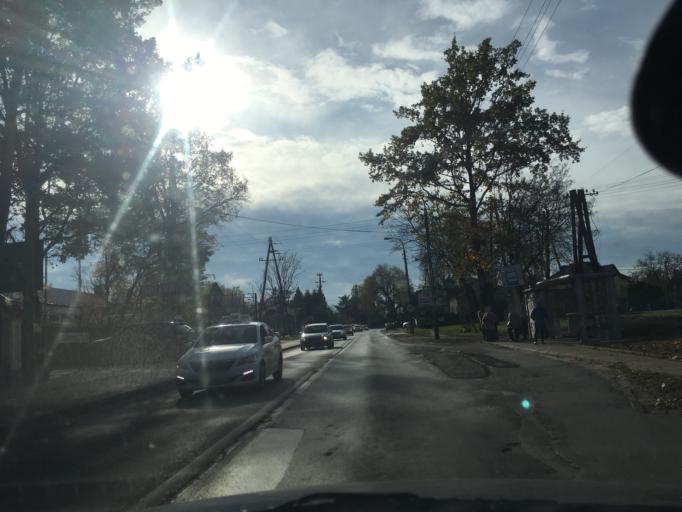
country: PL
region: Masovian Voivodeship
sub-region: Powiat piaseczynski
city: Piaseczno
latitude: 52.0570
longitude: 21.0083
